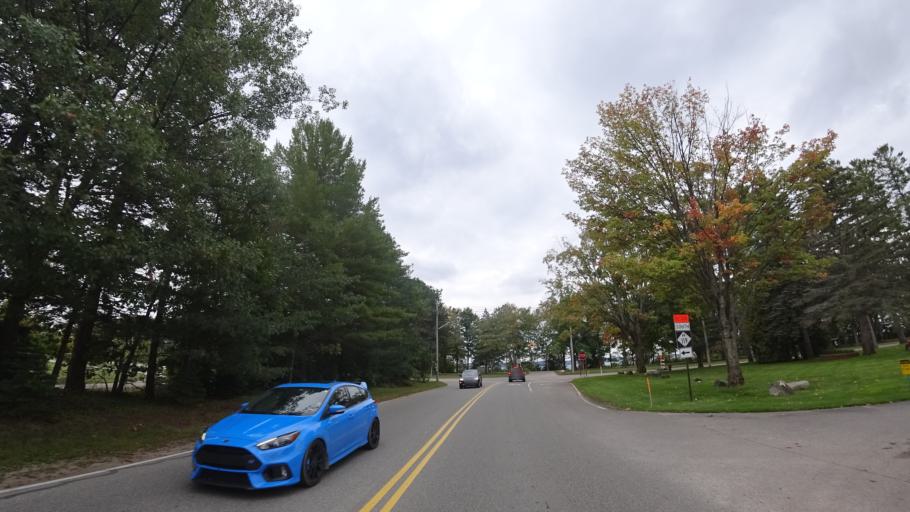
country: US
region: Michigan
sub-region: Emmet County
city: Harbor Springs
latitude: 45.4330
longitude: -84.9711
